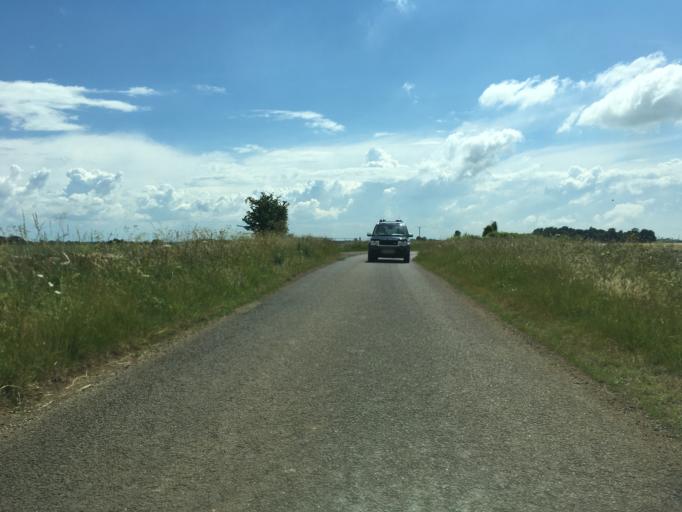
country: GB
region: England
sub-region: Gloucestershire
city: Coates
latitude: 51.7136
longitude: -2.0915
